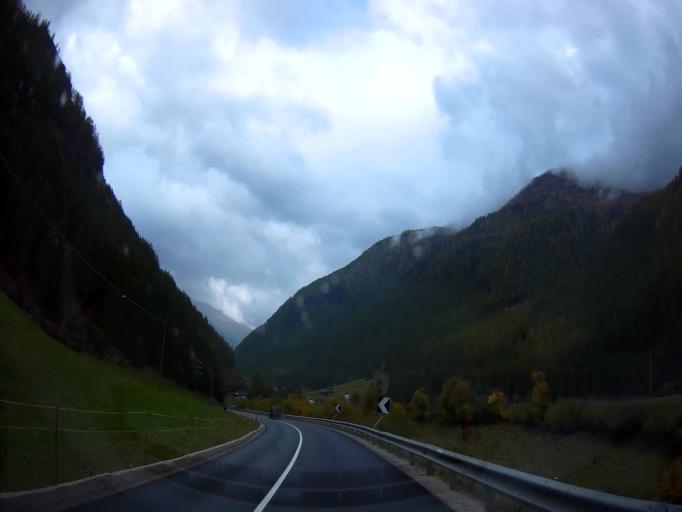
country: IT
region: Trentino-Alto Adige
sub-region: Bolzano
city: Senales
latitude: 46.7190
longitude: 10.8661
